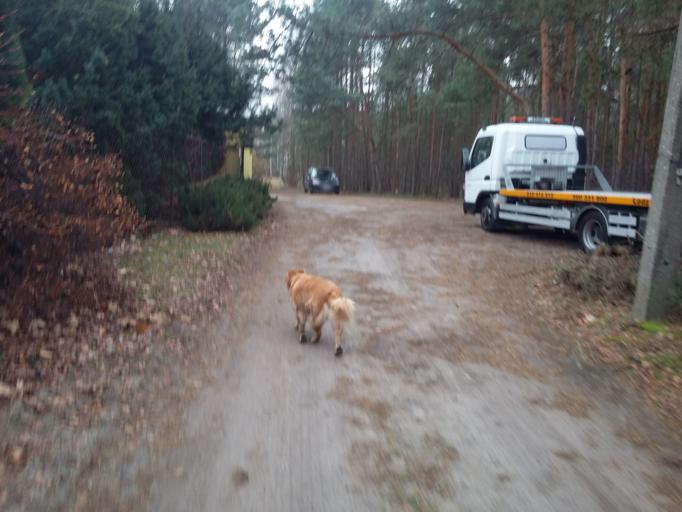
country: PL
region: Lodz Voivodeship
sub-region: Powiat pabianicki
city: Ksawerow
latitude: 51.7263
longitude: 19.3835
